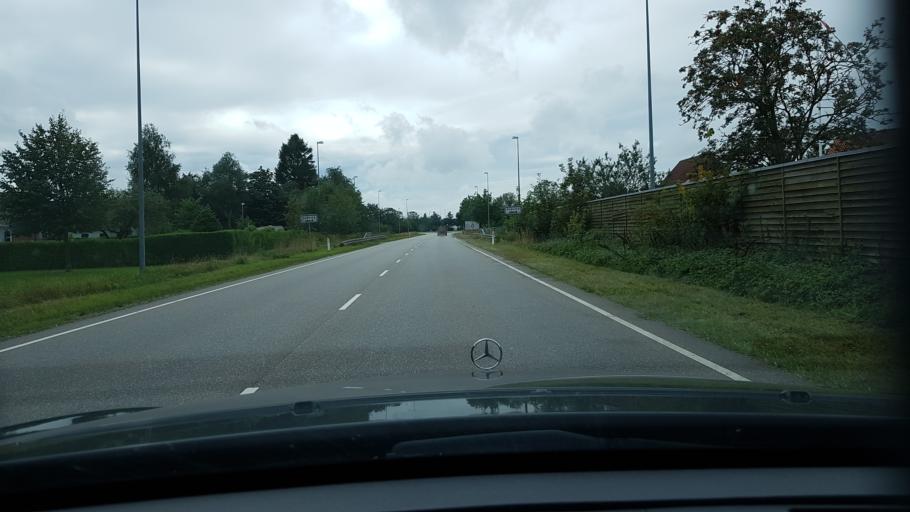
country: DK
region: North Denmark
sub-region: Mariagerfjord Kommune
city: Hadsund
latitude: 56.7227
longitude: 10.1286
